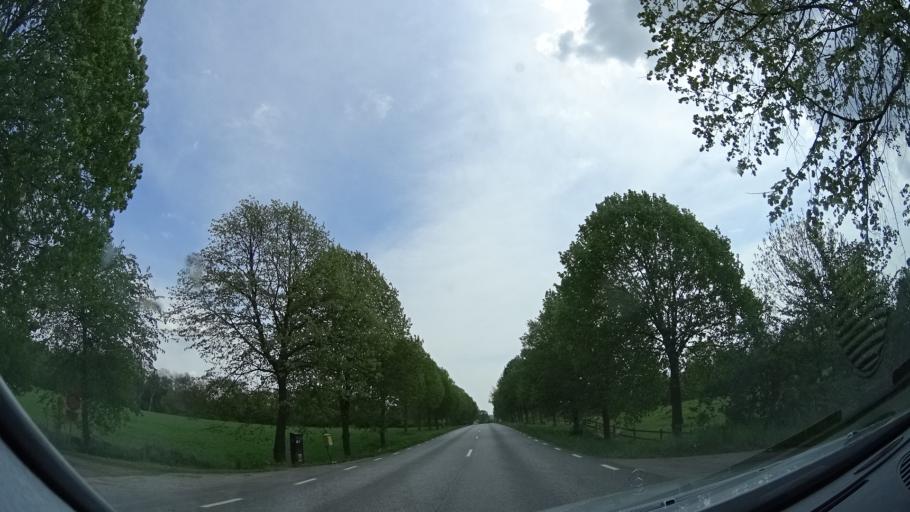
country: SE
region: Skane
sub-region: Hoors Kommun
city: Loberod
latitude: 55.7010
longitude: 13.5796
